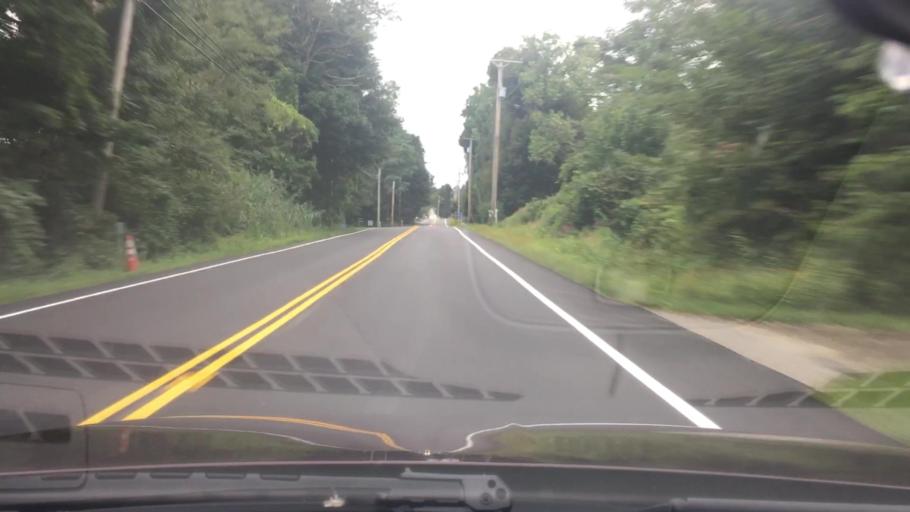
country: US
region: New York
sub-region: Dutchess County
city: Millbrook
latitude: 41.7942
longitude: -73.6542
